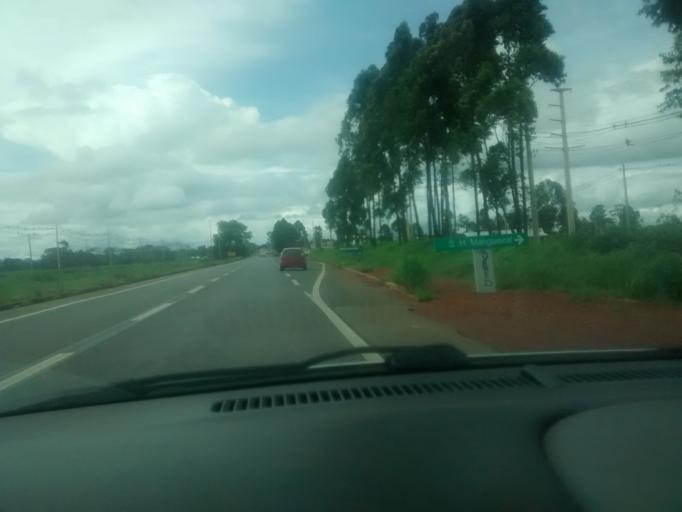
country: BR
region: Federal District
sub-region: Brasilia
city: Brasilia
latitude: -15.8901
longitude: -47.8206
